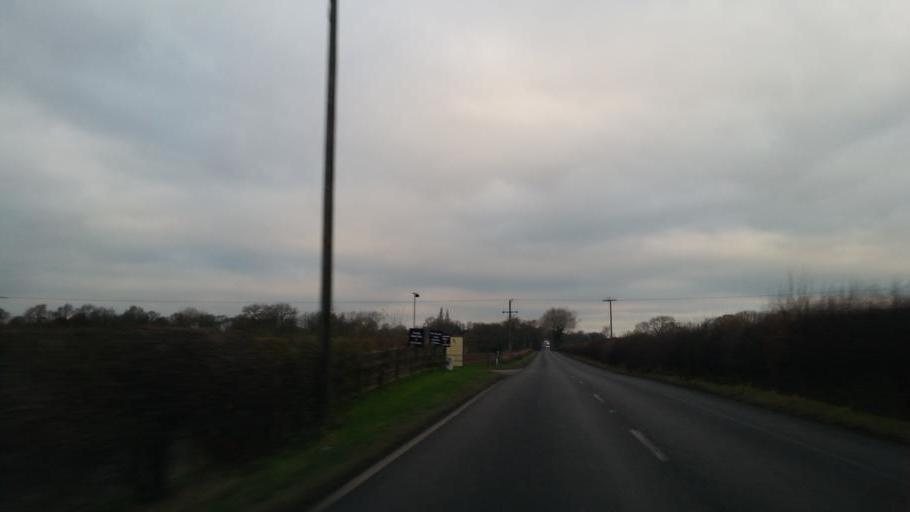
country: GB
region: England
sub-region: Nottinghamshire
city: Southwell
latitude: 53.1090
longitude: -0.9618
